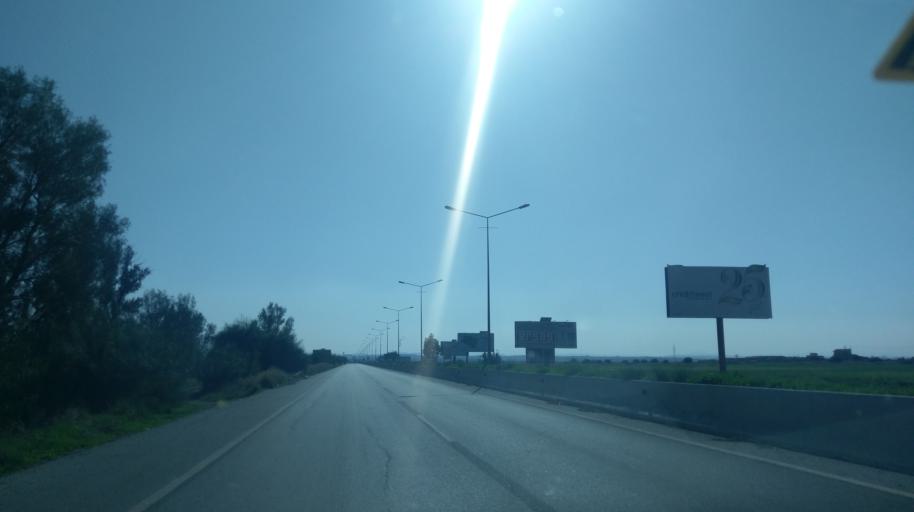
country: CY
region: Lefkosia
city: Geri
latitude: 35.2044
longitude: 33.4995
